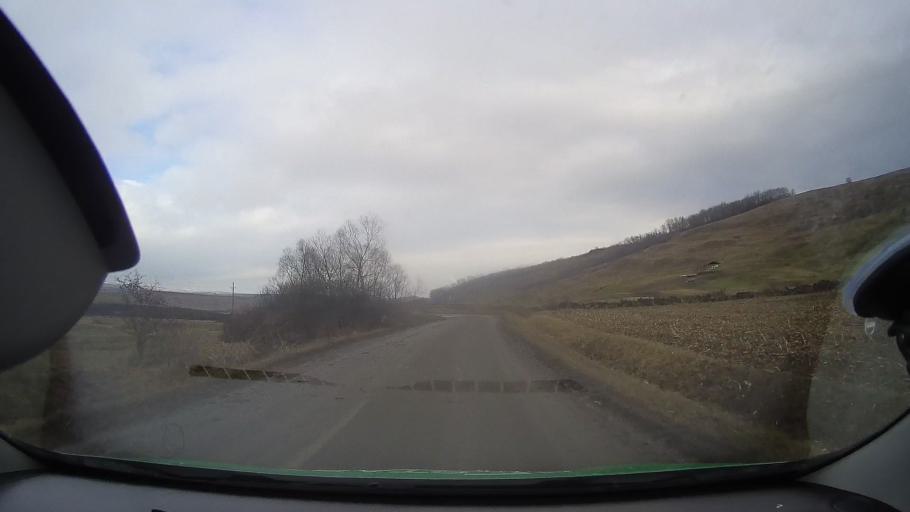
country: RO
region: Mures
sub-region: Comuna Ludus
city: Gheja
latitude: 46.4012
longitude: 24.0573
